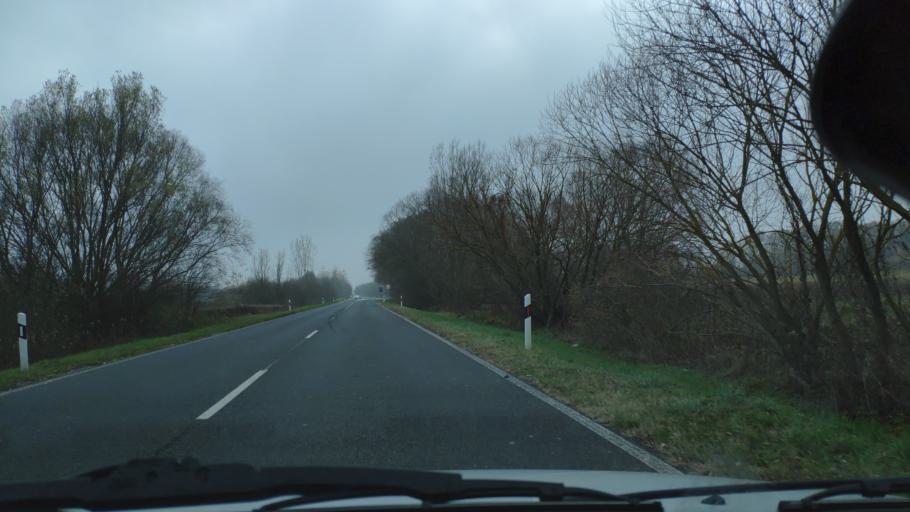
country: HU
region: Somogy
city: Balatonbereny
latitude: 46.6064
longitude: 17.2701
